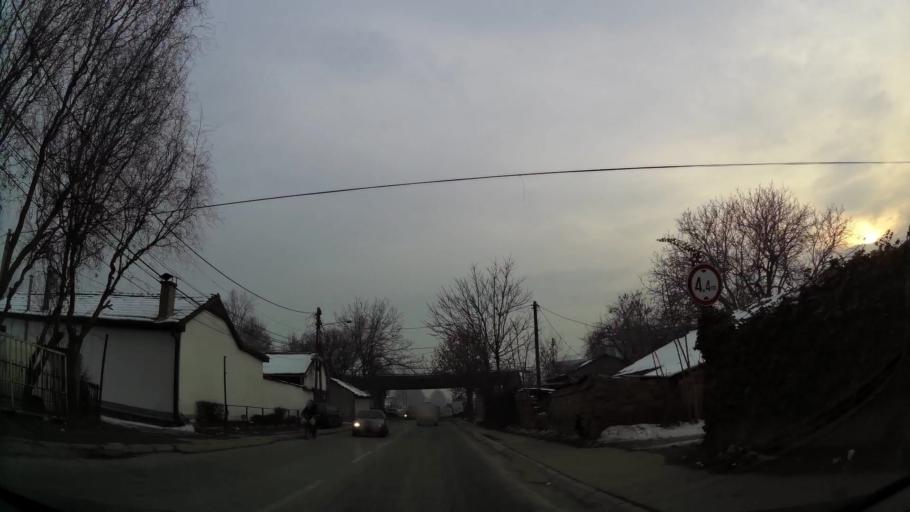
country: MK
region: Suto Orizari
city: Suto Orizare
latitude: 42.0281
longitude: 21.4291
